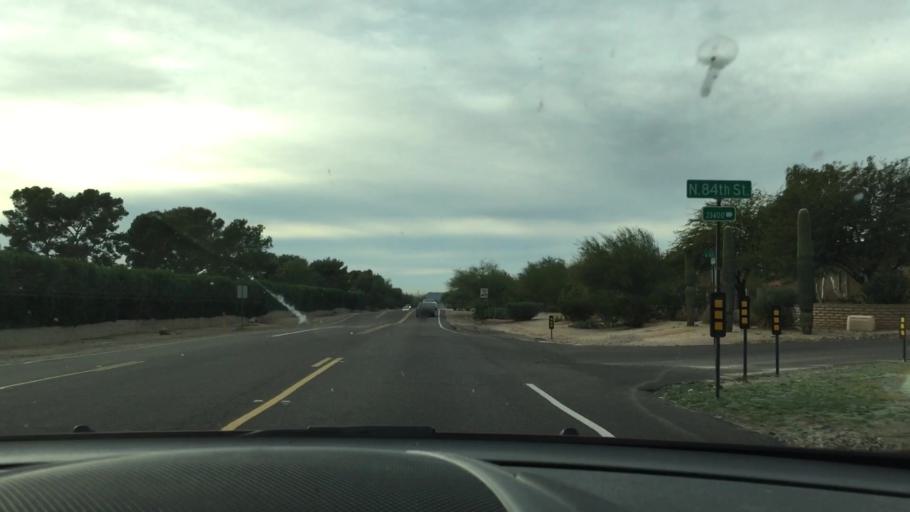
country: US
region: Arizona
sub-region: Maricopa County
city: Carefree
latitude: 33.6987
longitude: -111.8992
